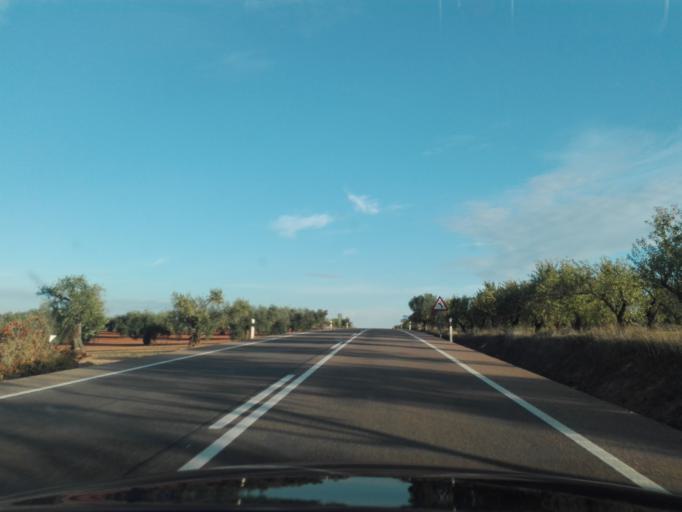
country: ES
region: Extremadura
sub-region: Provincia de Badajoz
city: Usagre
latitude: 38.3461
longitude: -6.1847
